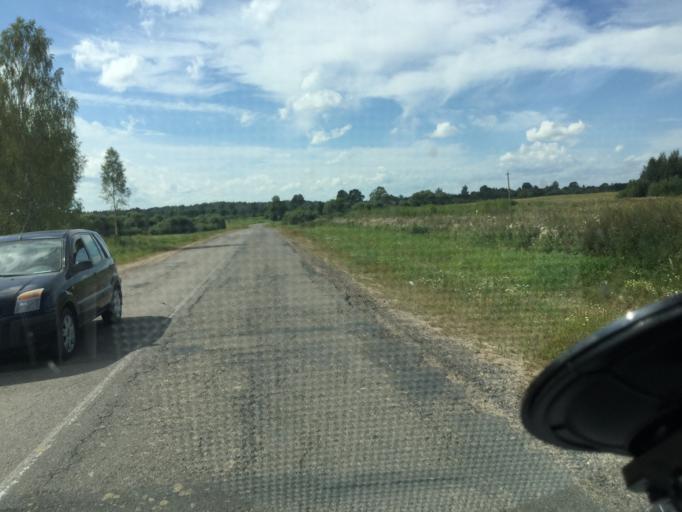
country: BY
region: Vitebsk
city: Chashniki
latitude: 55.3114
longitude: 29.4149
